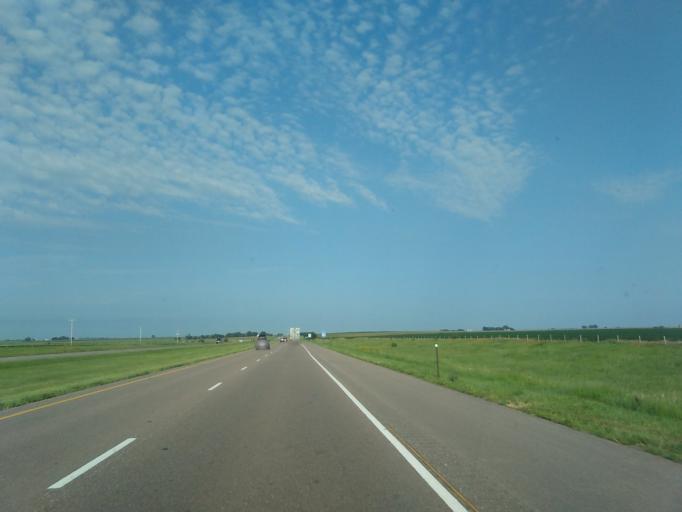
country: US
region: Nebraska
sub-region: York County
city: York
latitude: 40.8212
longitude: -97.6850
